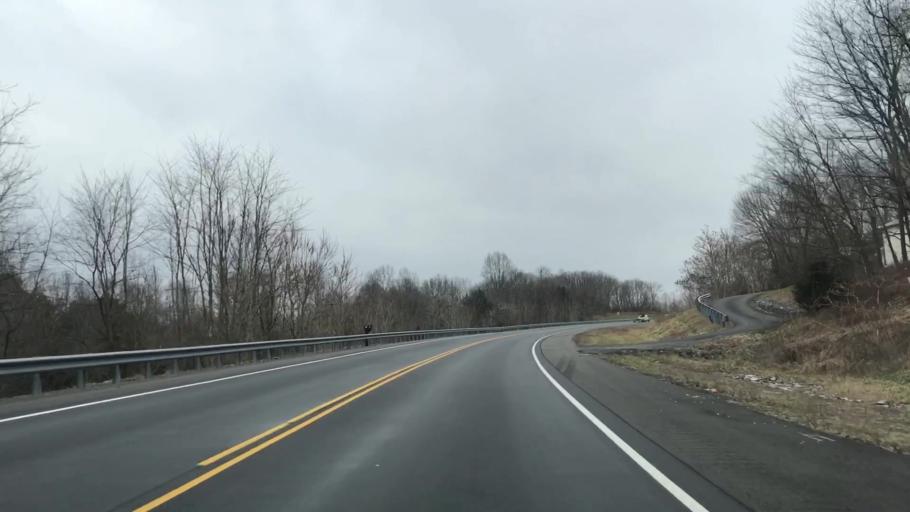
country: US
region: Kentucky
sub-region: Adair County
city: Columbia
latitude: 36.9736
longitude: -85.4214
